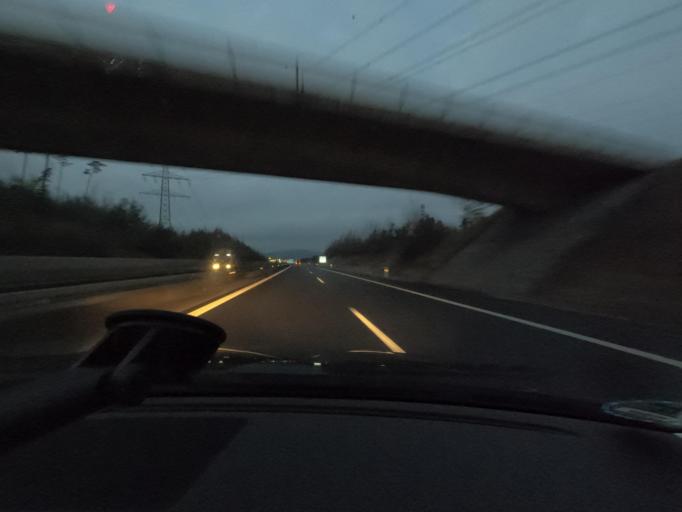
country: DE
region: Bavaria
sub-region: Upper Franconia
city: Rodental
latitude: 50.2724
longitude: 11.0173
